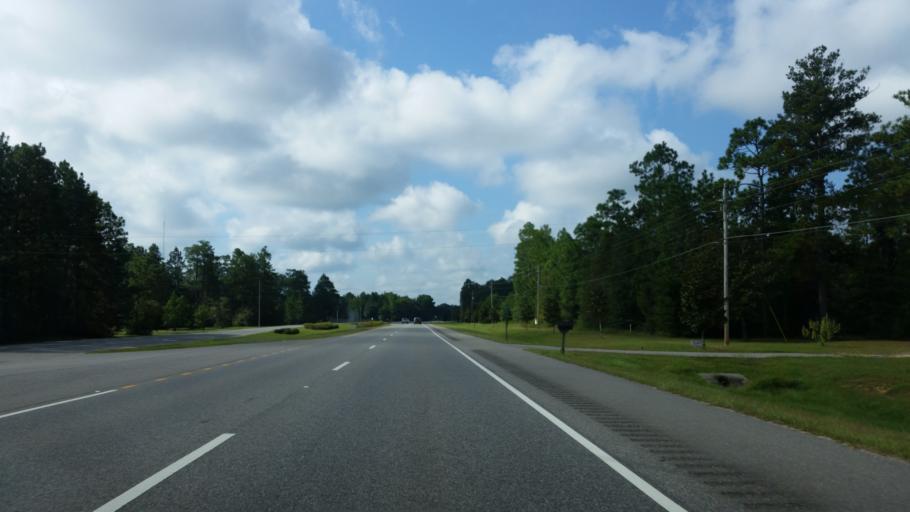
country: US
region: Alabama
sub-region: Baldwin County
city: Bay Minette
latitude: 30.9205
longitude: -87.7749
